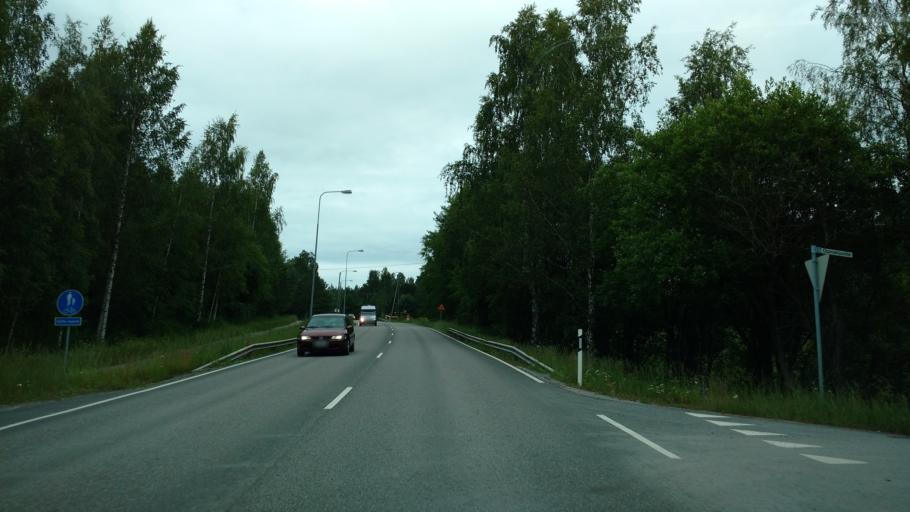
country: FI
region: Varsinais-Suomi
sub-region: Salo
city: Halikko
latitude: 60.4344
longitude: 23.0471
